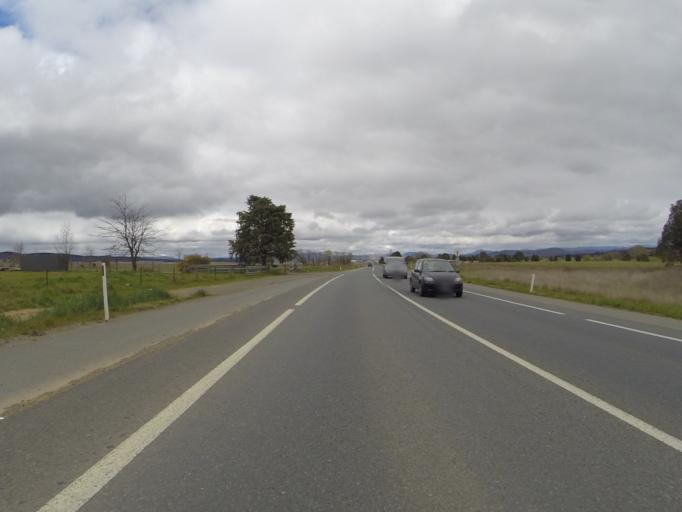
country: AU
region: Australian Capital Territory
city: Canberra
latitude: -35.2671
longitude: 149.1965
